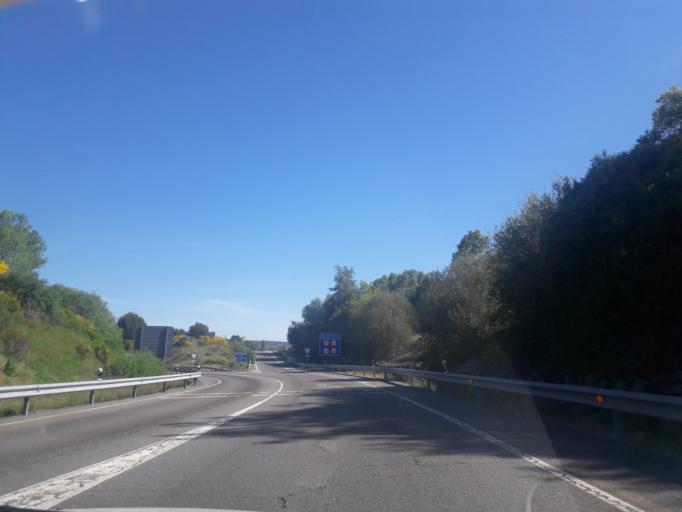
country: ES
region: Castille and Leon
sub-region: Provincia de Salamanca
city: Puerto de Bejar
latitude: 40.3469
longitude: -5.8444
